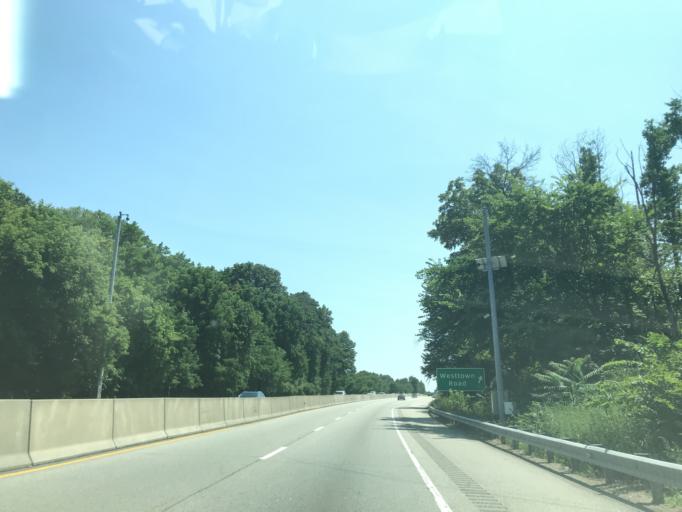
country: US
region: Pennsylvania
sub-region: Chester County
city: West Chester
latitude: 39.9600
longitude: -75.5799
